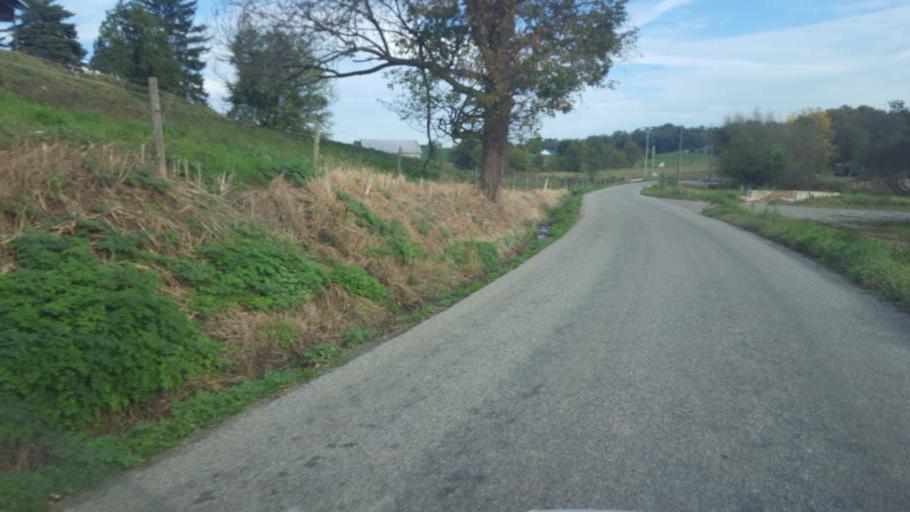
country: US
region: Ohio
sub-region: Holmes County
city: Millersburg
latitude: 40.5726
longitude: -81.8063
